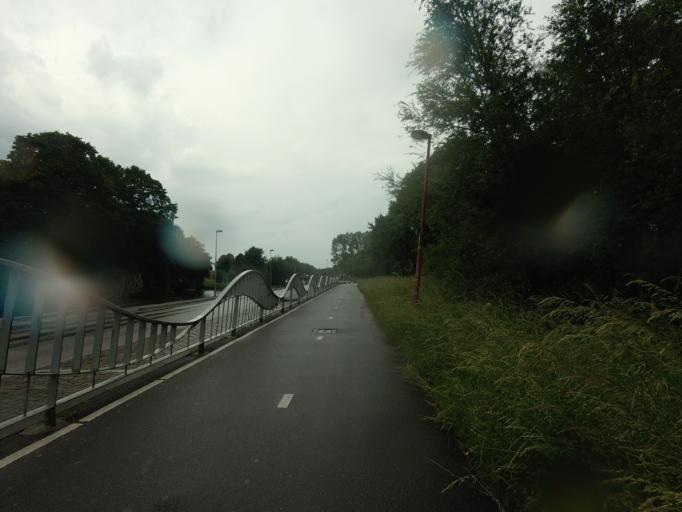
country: NL
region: Utrecht
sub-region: Gemeente Utrecht
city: Utrecht
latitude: 52.1130
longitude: 5.1000
